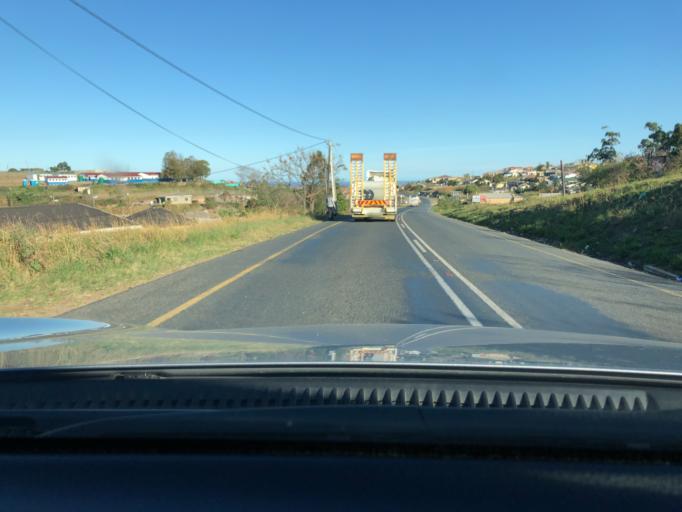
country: ZA
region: KwaZulu-Natal
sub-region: eThekwini Metropolitan Municipality
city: Umkomaas
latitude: -30.0049
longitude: 30.8022
